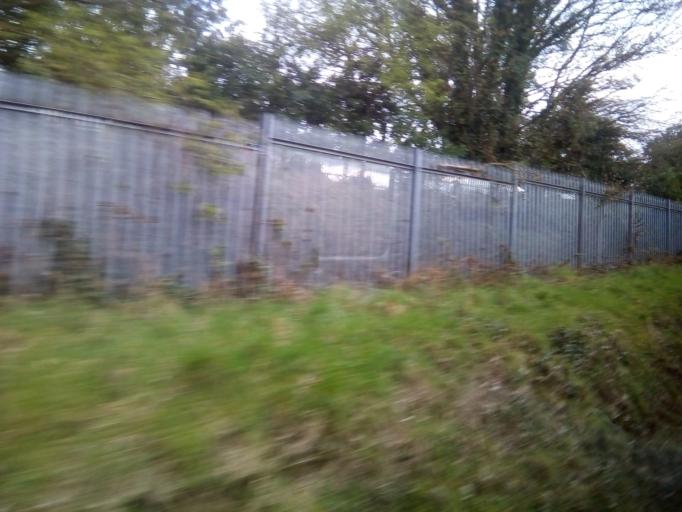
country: IE
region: Leinster
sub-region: An Iarmhi
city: An Muileann gCearr
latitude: 53.5302
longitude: -7.3471
